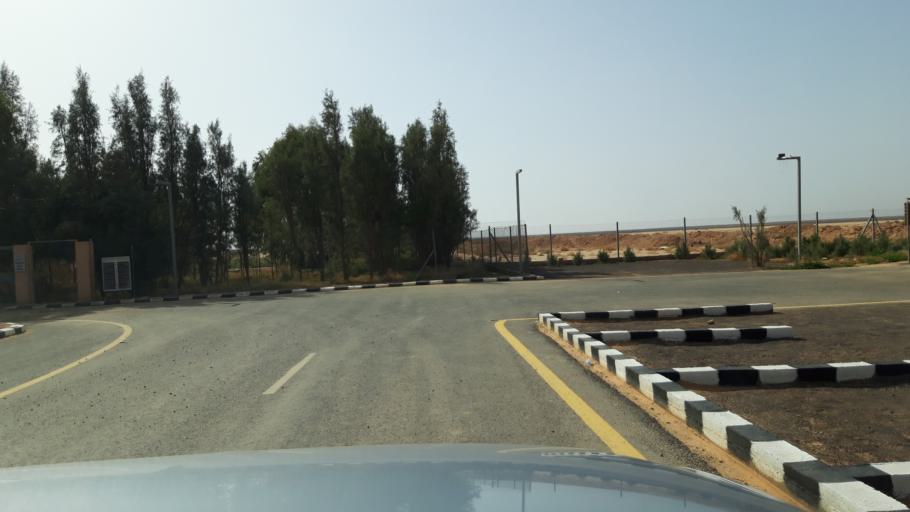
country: JO
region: Amman
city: Al Azraq ash Shamali
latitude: 31.7522
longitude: 36.7553
